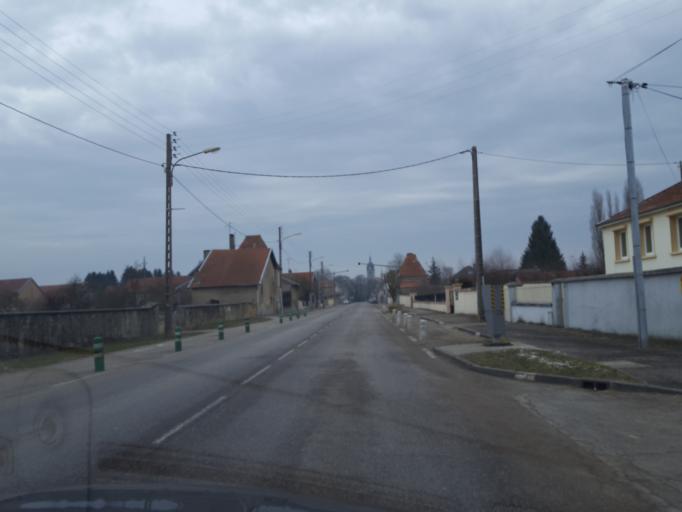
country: FR
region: Lorraine
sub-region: Departement de la Meuse
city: Etain
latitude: 49.2130
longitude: 5.6253
